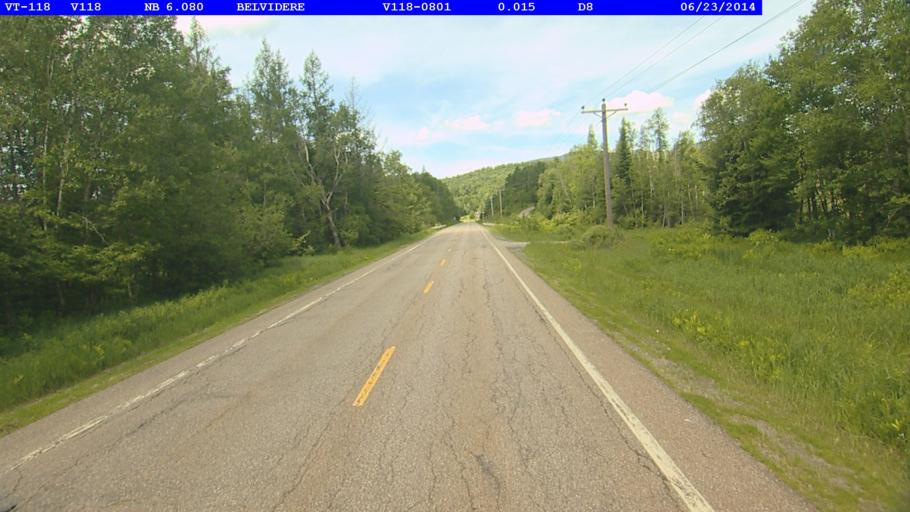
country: US
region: Vermont
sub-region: Lamoille County
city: Johnson
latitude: 44.7649
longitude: -72.6152
